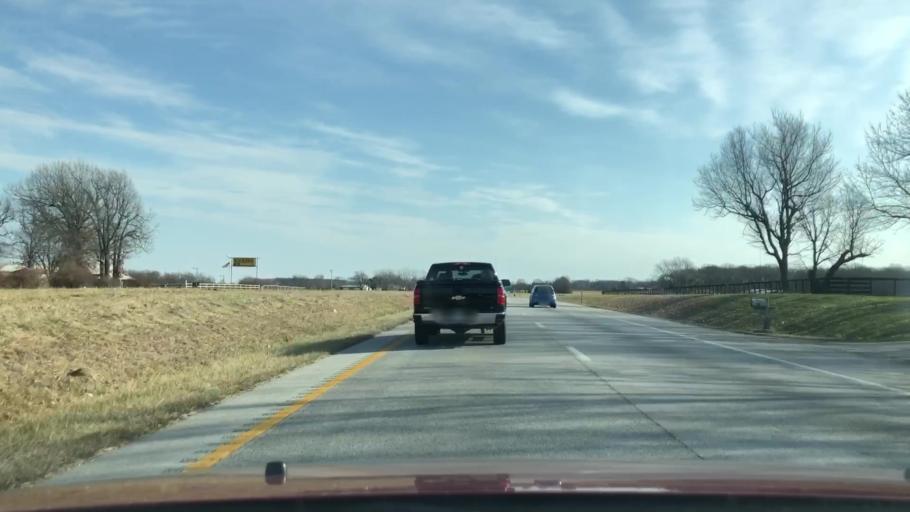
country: US
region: Missouri
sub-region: Webster County
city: Rogersville
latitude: 37.1184
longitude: -93.1095
